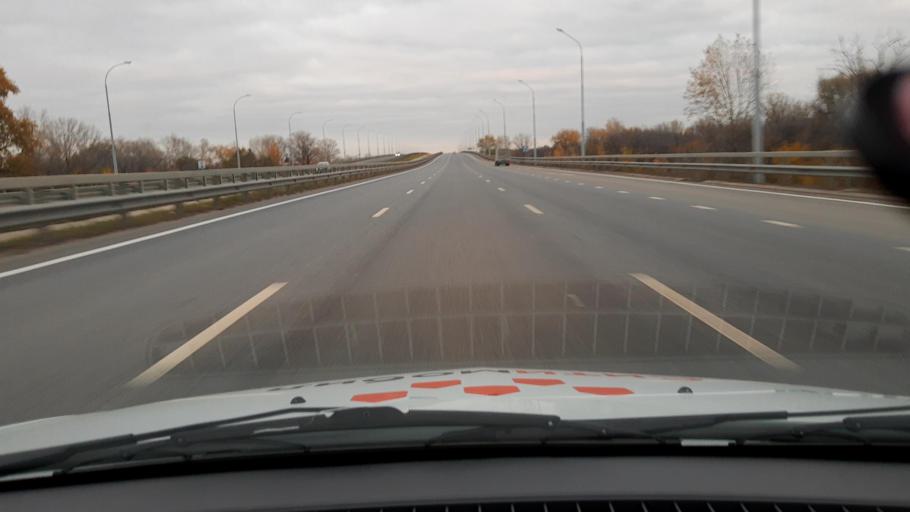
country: RU
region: Bashkortostan
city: Ufa
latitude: 54.6447
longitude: 55.9893
